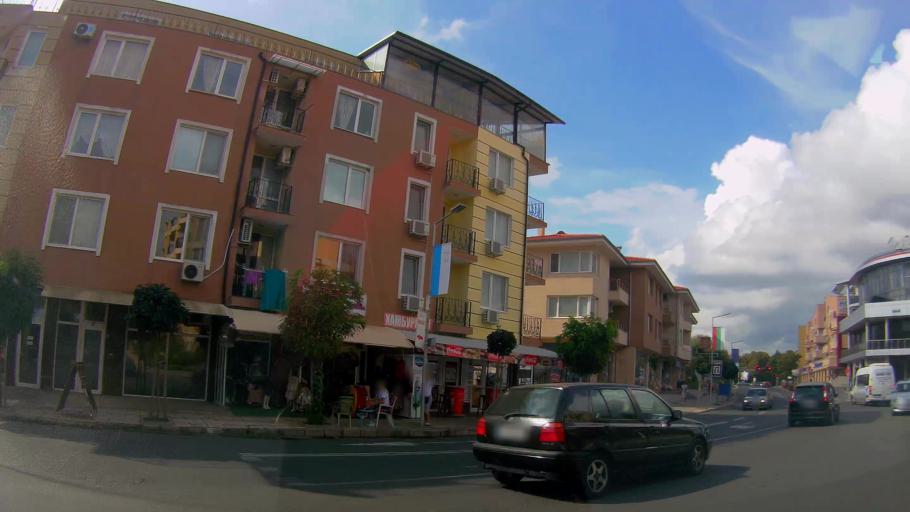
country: BG
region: Burgas
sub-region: Obshtina Primorsko
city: Primorsko
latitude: 42.2663
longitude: 27.7486
